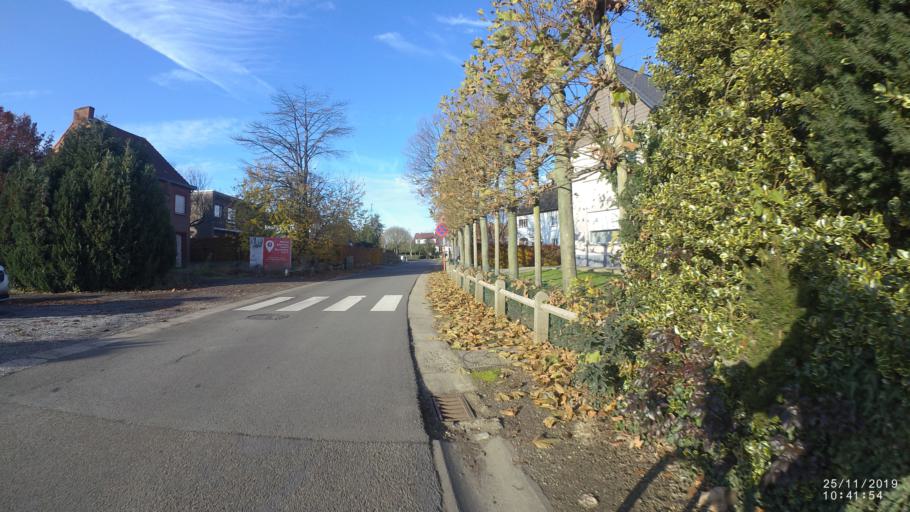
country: BE
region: Flanders
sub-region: Provincie Vlaams-Brabant
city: Scherpenheuvel-Zichem
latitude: 51.0112
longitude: 4.9499
